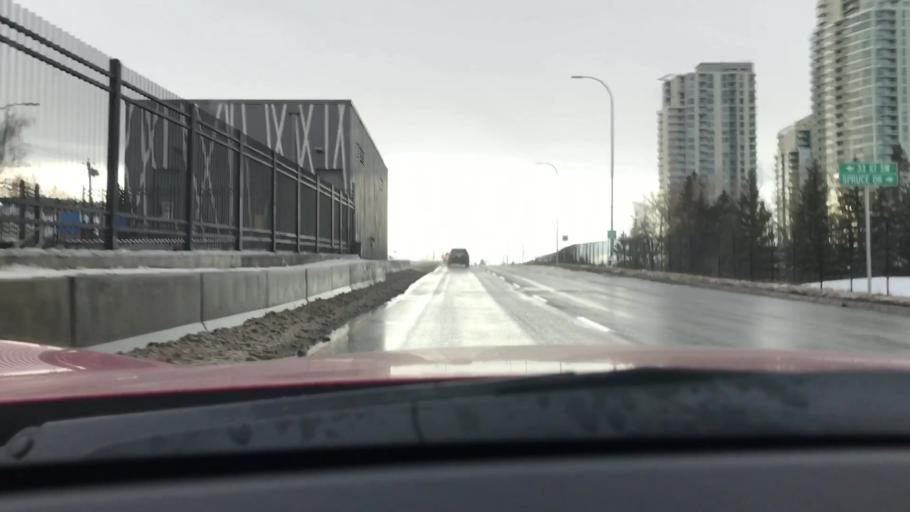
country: CA
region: Alberta
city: Calgary
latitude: 51.0417
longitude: -114.1319
